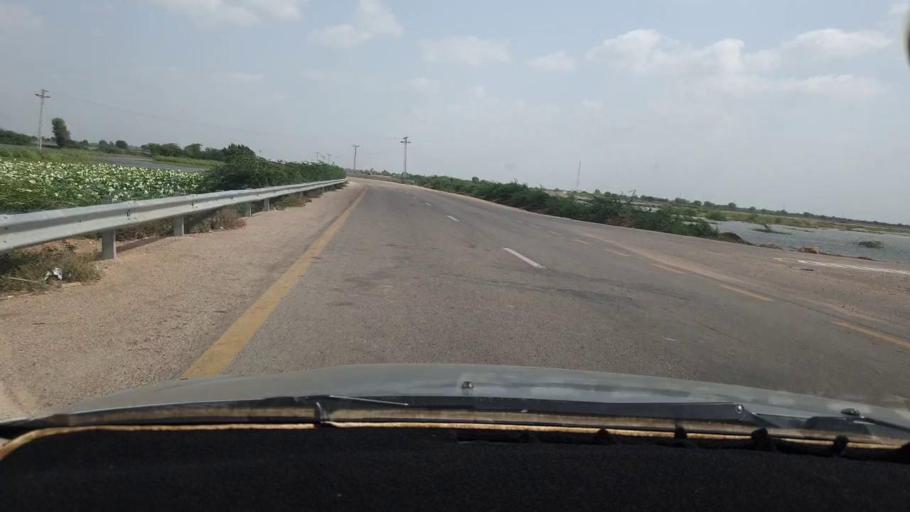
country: PK
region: Sindh
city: Naukot
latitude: 25.0007
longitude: 69.2855
